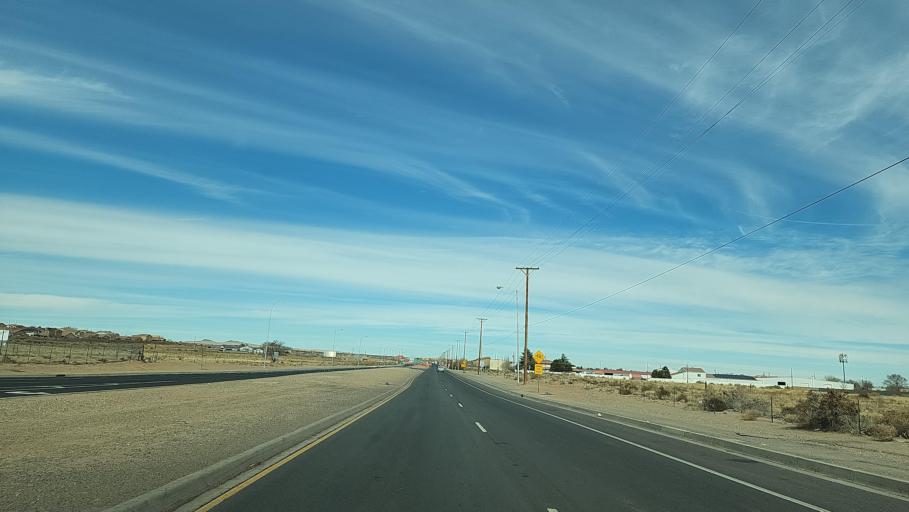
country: US
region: New Mexico
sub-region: Bernalillo County
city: South Valley
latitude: 35.0607
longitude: -106.7079
